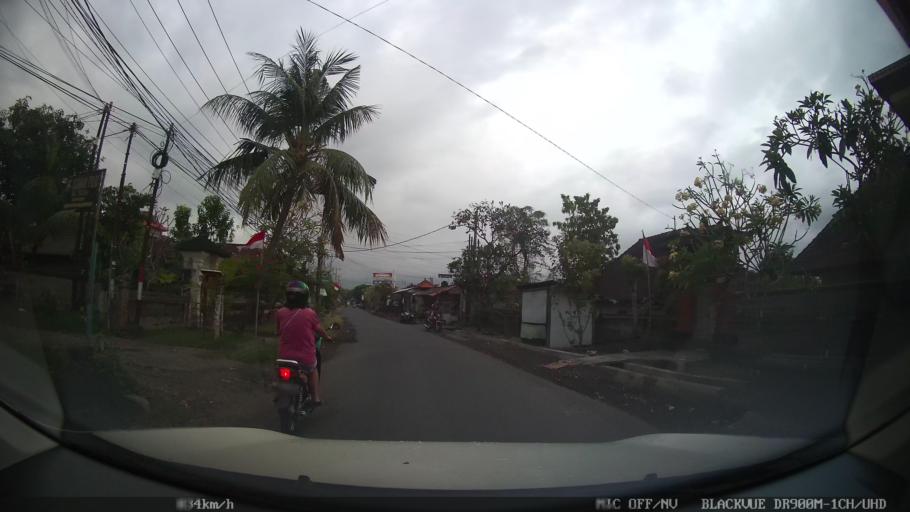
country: ID
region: Bali
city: Banjar Kertajiwa
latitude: -8.6381
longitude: 115.2659
